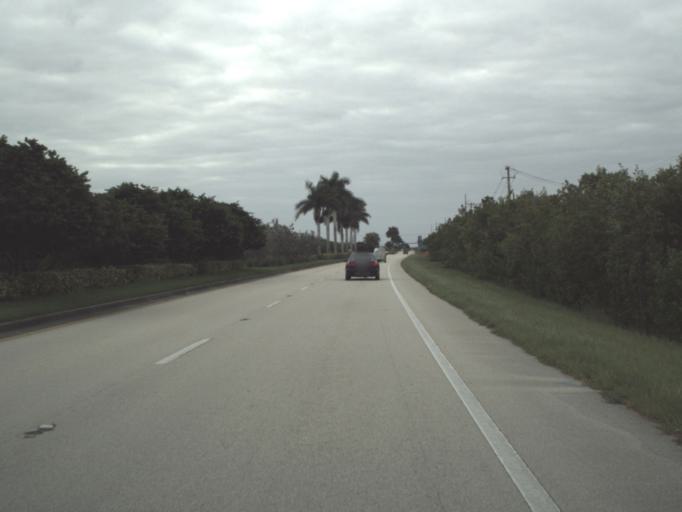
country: US
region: Florida
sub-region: Collier County
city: Marco
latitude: 26.0019
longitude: -81.7018
